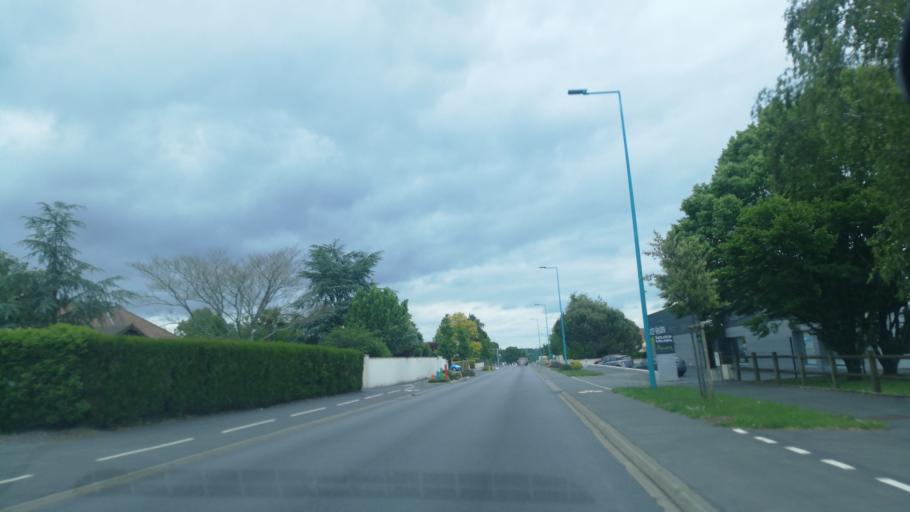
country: FR
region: Poitou-Charentes
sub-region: Departement des Deux-Sevres
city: Moncoutant
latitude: 46.7280
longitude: -0.5839
